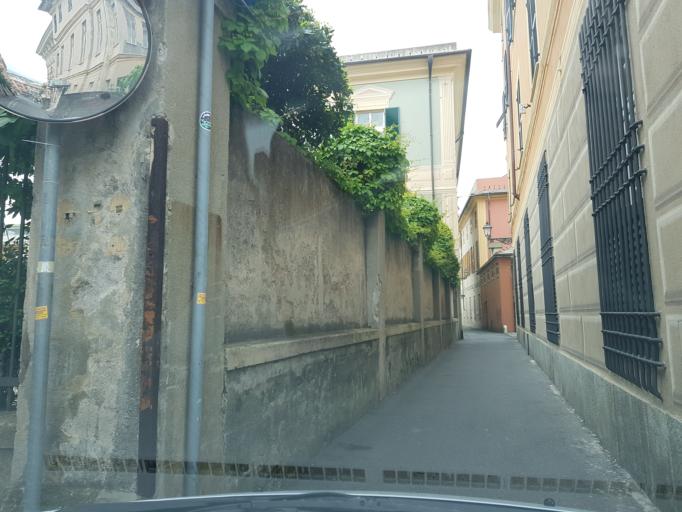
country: IT
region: Liguria
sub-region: Provincia di Genova
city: San Teodoro
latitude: 44.3984
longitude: 8.9578
